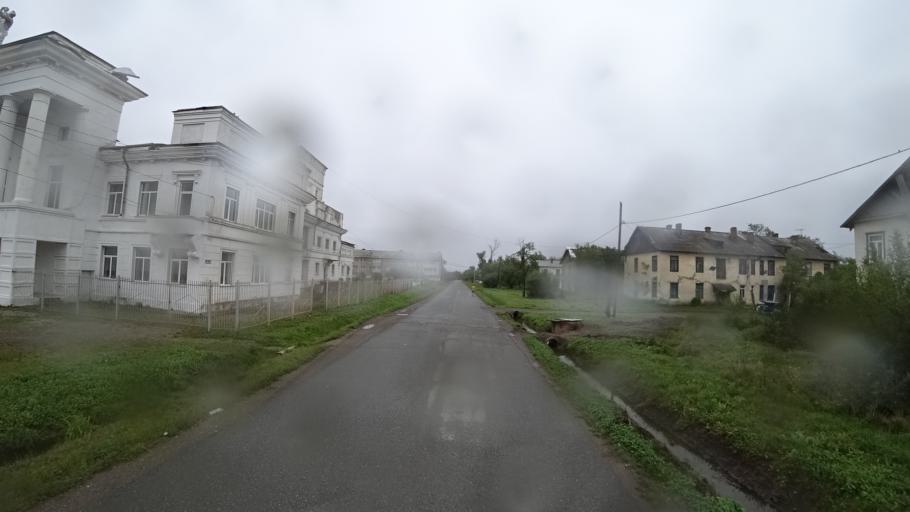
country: RU
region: Primorskiy
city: Monastyrishche
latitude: 44.1966
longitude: 132.4272
